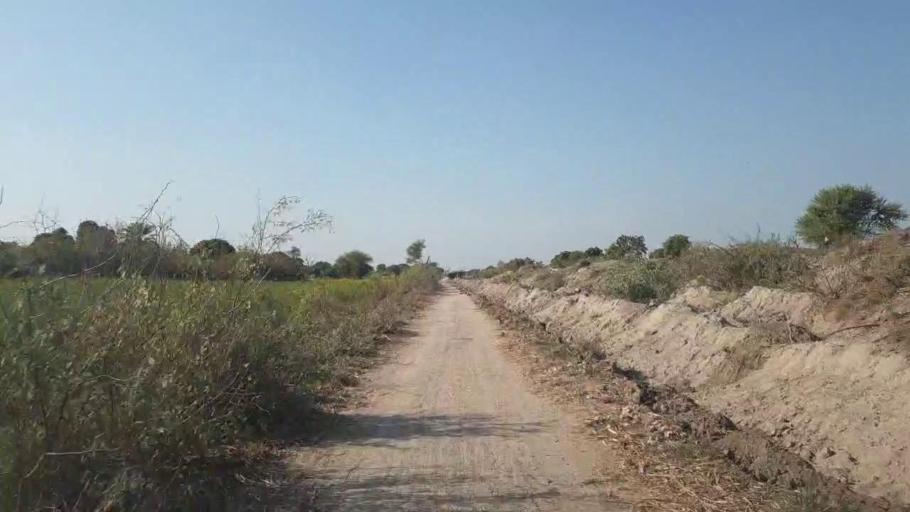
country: PK
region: Sindh
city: Chambar
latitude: 25.3043
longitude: 68.7852
